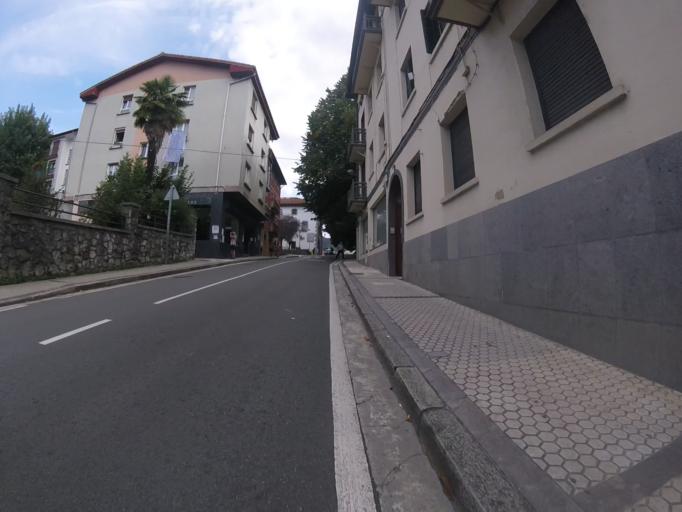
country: ES
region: Basque Country
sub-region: Provincia de Guipuzcoa
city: Andoain
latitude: 43.2189
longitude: -2.0201
